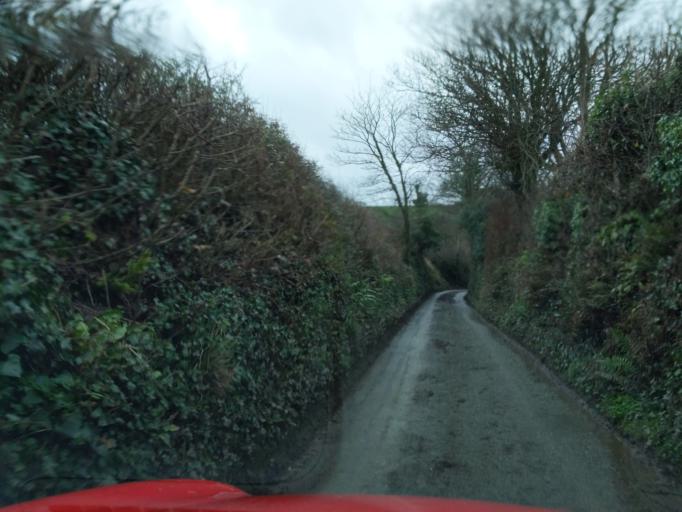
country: GB
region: England
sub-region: Cornwall
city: Fowey
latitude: 50.3380
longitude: -4.5805
